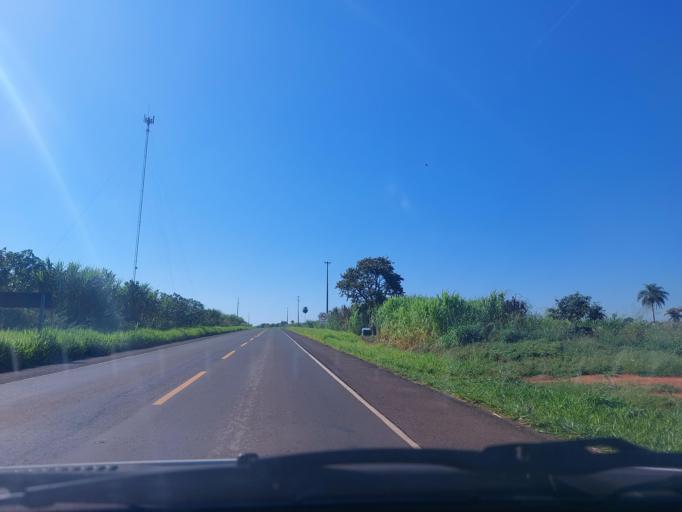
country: PY
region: San Pedro
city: Guayaybi
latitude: -24.3175
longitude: -56.1715
